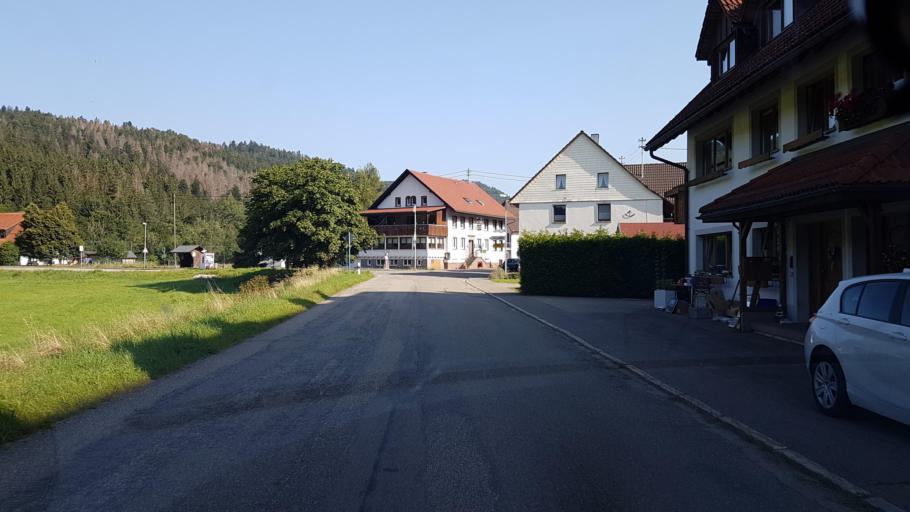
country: DE
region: Baden-Wuerttemberg
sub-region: Freiburg Region
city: Dachsberg
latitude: 47.6950
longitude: 8.1247
